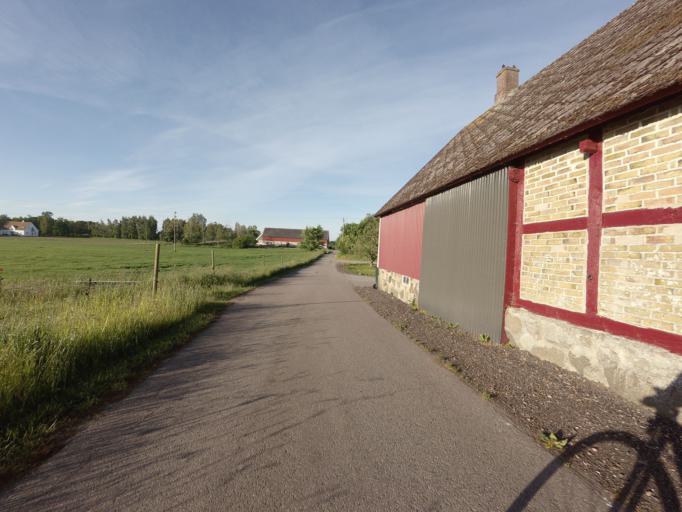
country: SE
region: Skane
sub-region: Hoganas Kommun
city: Hoganas
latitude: 56.2443
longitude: 12.6506
